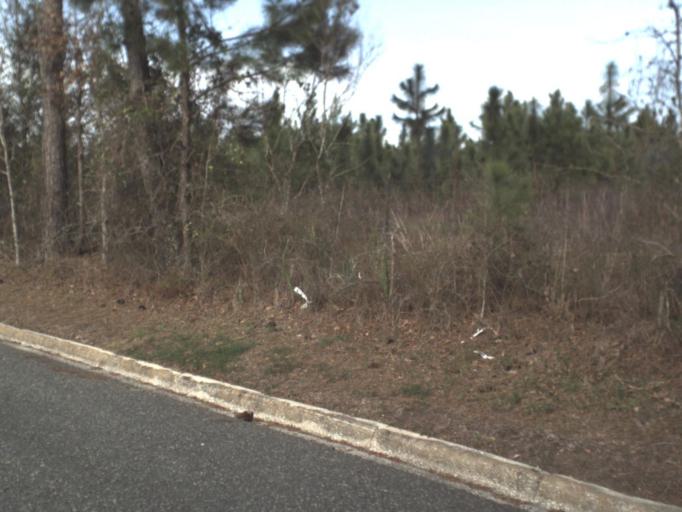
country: US
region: Florida
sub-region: Jefferson County
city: Monticello
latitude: 30.4142
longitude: -83.9111
